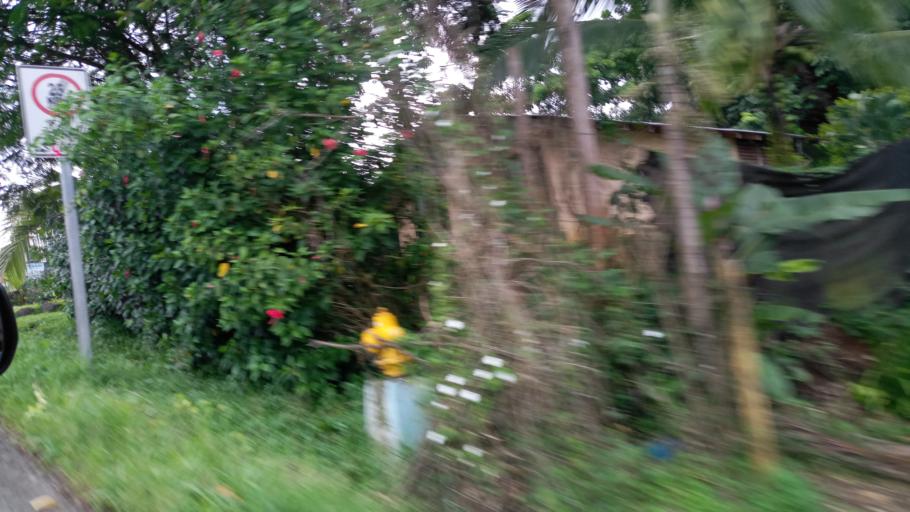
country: CR
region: Alajuela
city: Pocosol
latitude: 10.3629
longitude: -84.5887
